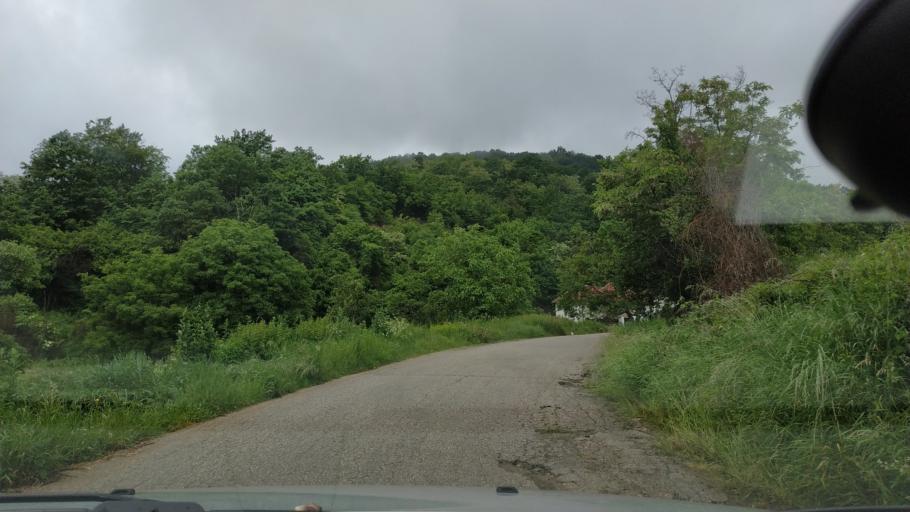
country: RS
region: Central Serbia
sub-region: Toplicki Okrug
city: Prokuplje
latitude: 43.3919
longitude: 21.5535
